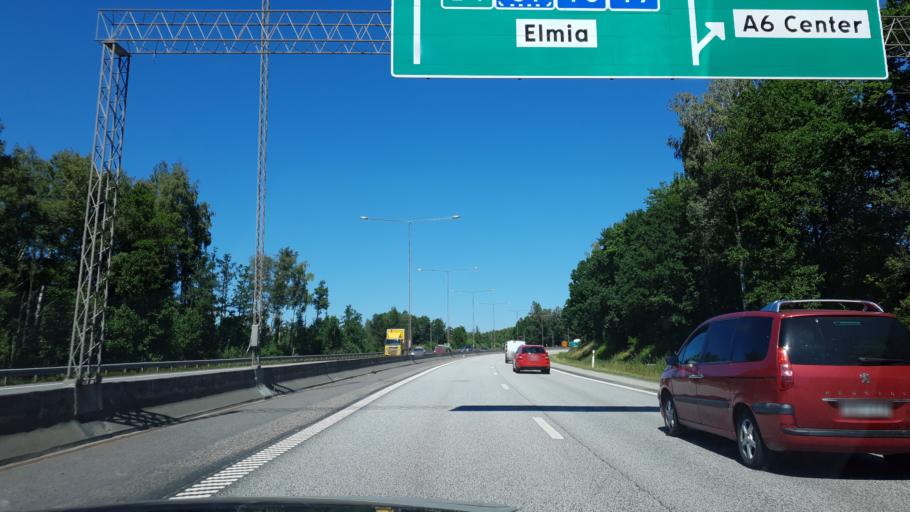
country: SE
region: Joenkoeping
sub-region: Jonkopings Kommun
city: Jonkoping
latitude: 57.7684
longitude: 14.1894
